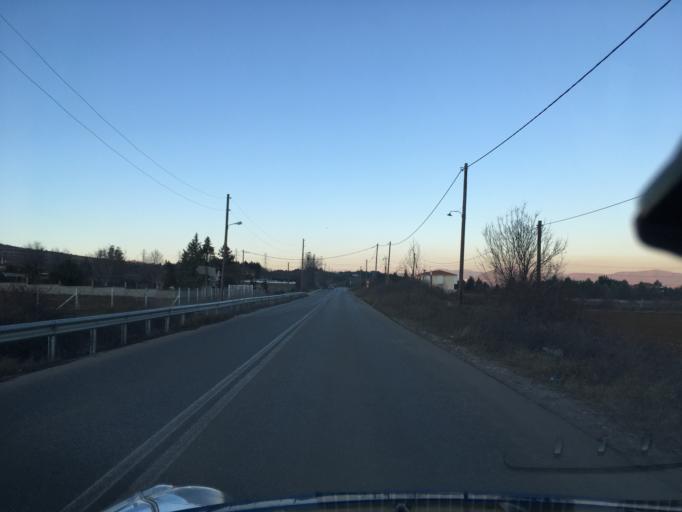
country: GR
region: West Macedonia
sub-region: Nomos Kozanis
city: Kozani
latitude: 40.2567
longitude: 21.7583
